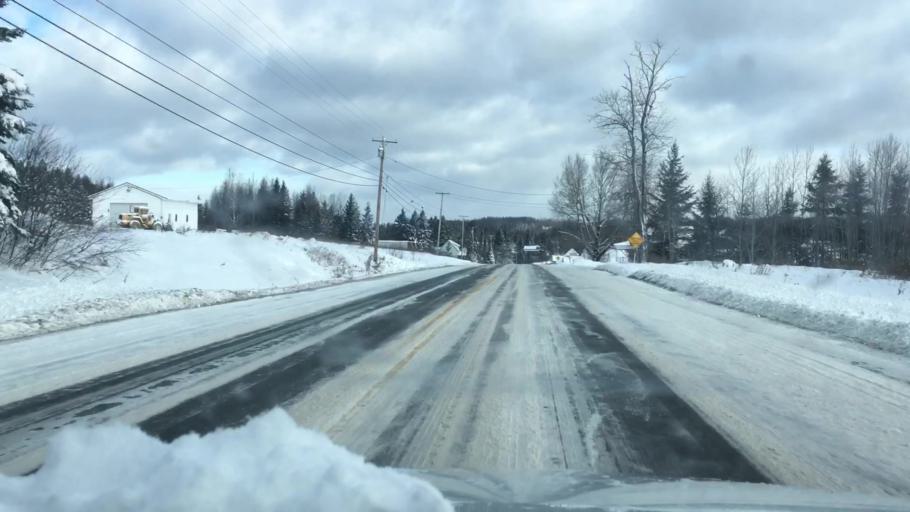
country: US
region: Maine
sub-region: Aroostook County
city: Caribou
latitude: 46.9741
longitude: -68.0358
